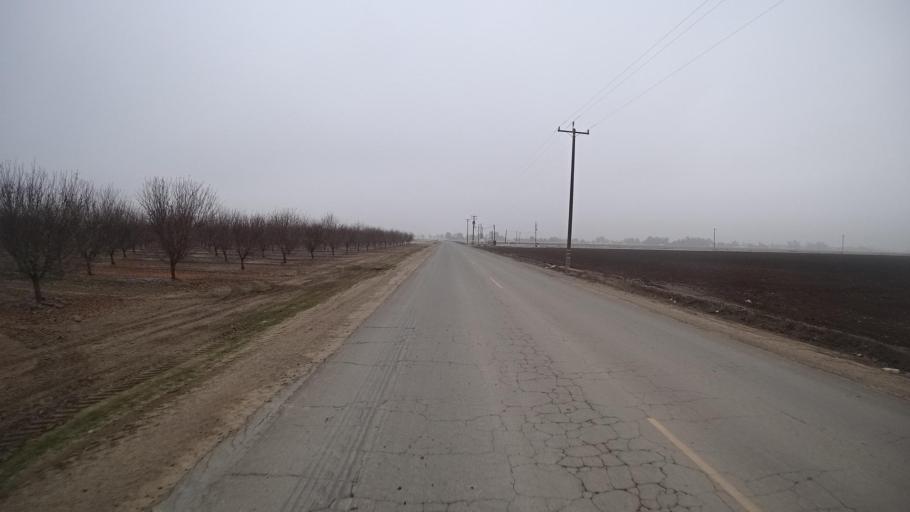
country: US
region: California
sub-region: Kern County
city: Greenfield
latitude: 35.2379
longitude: -119.0319
